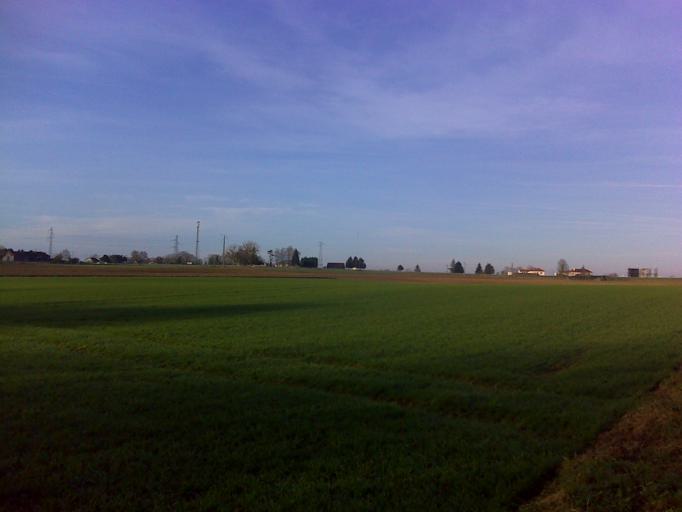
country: FR
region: Champagne-Ardenne
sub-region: Departement de l'Aube
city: Lusigny-sur-Barse
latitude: 48.2440
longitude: 4.3294
